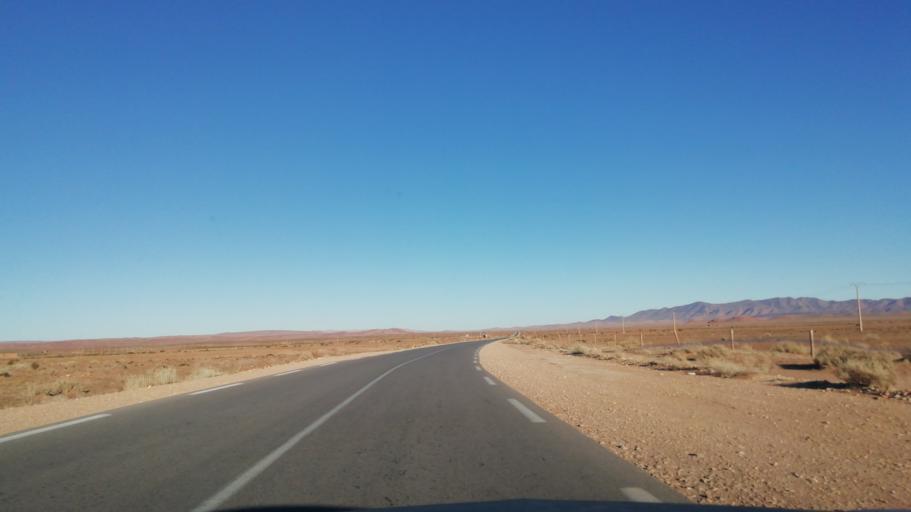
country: DZ
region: El Bayadh
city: El Abiodh Sidi Cheikh
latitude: 33.1727
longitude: 0.5190
